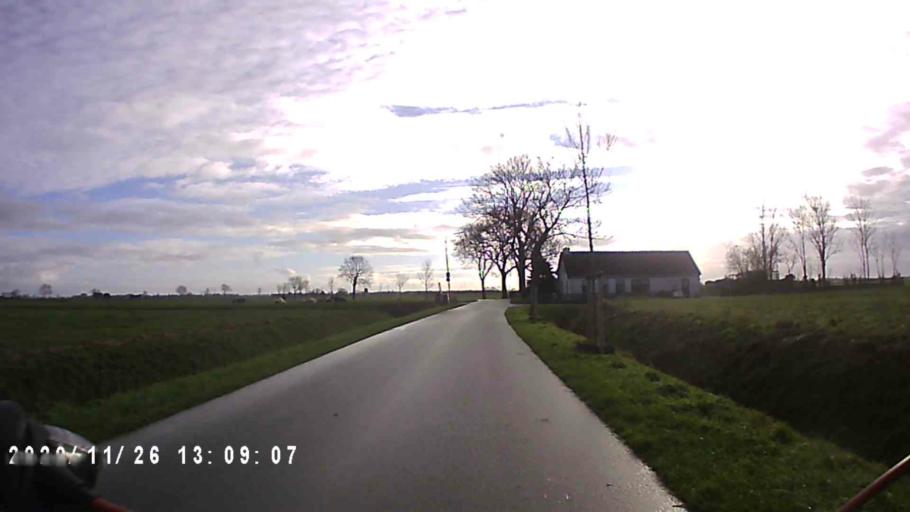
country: NL
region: Groningen
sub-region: Gemeente Appingedam
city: Appingedam
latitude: 53.3519
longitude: 6.8521
